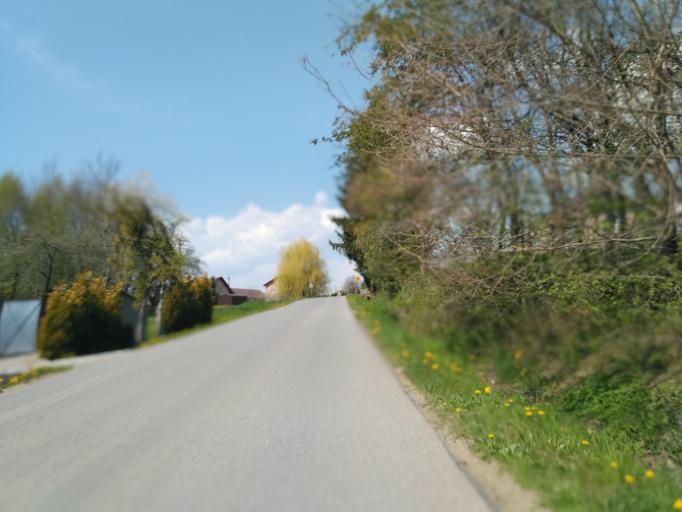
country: PL
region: Subcarpathian Voivodeship
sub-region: Powiat jasielski
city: Osiek Jasielski
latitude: 49.6873
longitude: 21.5218
